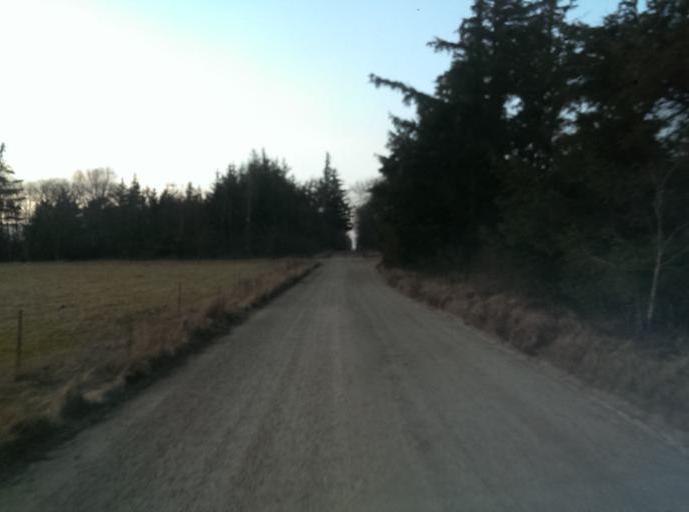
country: DK
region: South Denmark
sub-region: Varde Kommune
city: Oksbol
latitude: 55.5607
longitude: 8.3153
